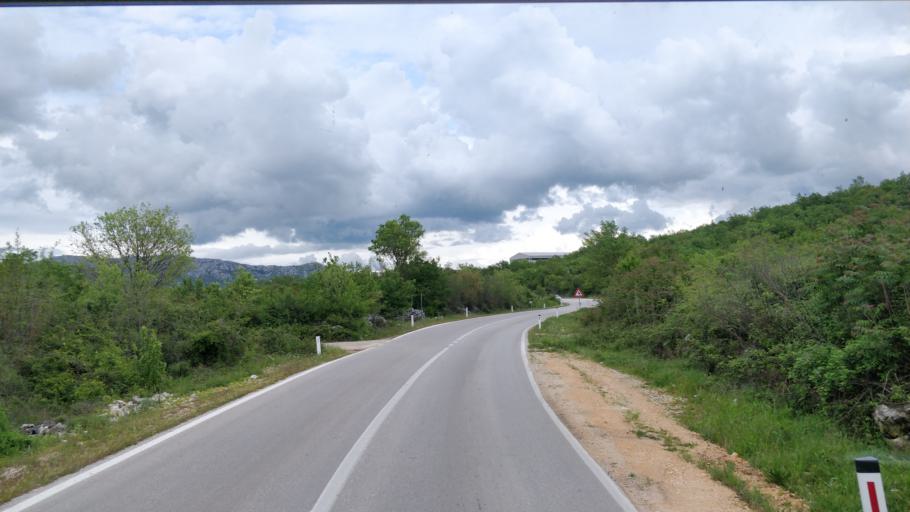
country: BA
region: Federation of Bosnia and Herzegovina
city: Ljubuski
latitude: 43.1783
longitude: 17.5071
